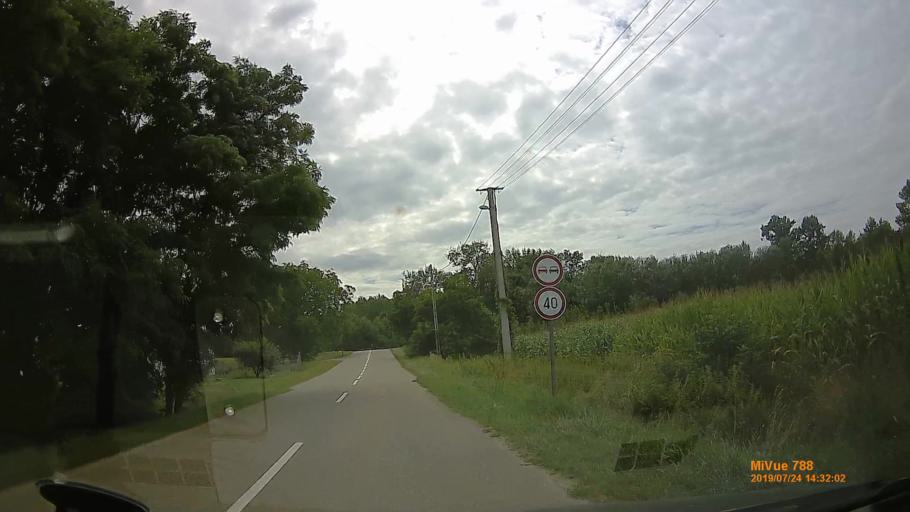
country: HU
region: Szabolcs-Szatmar-Bereg
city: Mandok
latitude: 48.3183
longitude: 22.2557
